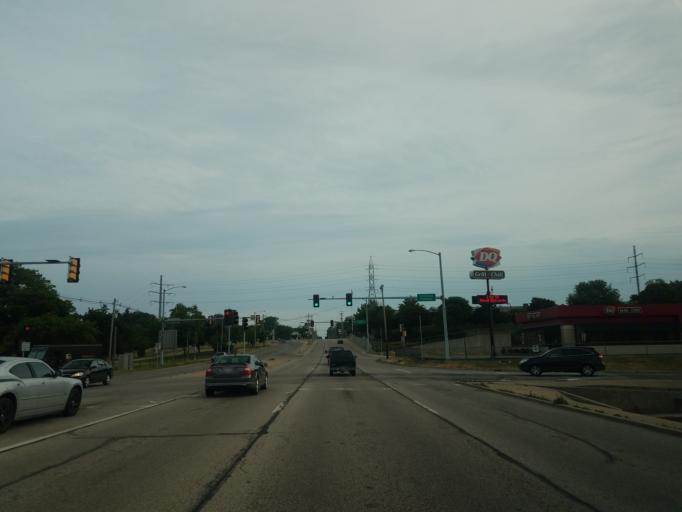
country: US
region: Illinois
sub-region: McLean County
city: Bloomington
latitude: 40.4595
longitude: -88.9928
